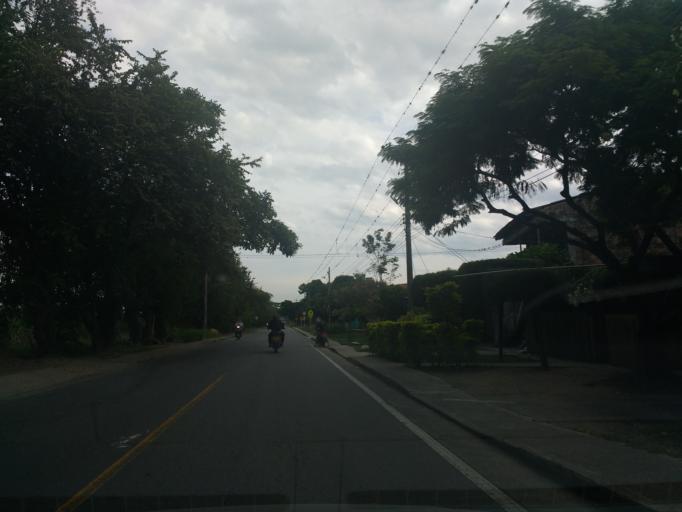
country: CO
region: Cauca
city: Miranda
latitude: 3.2851
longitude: -76.2249
